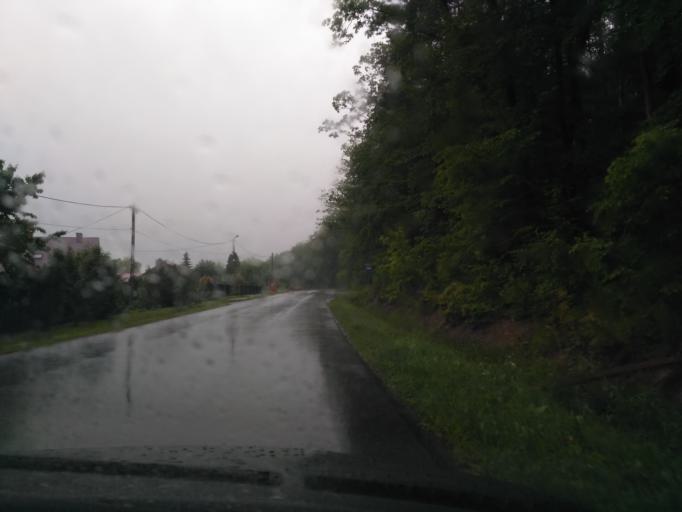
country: PL
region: Subcarpathian Voivodeship
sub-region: Powiat jasielski
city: Debowiec
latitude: 49.6585
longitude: 21.4233
